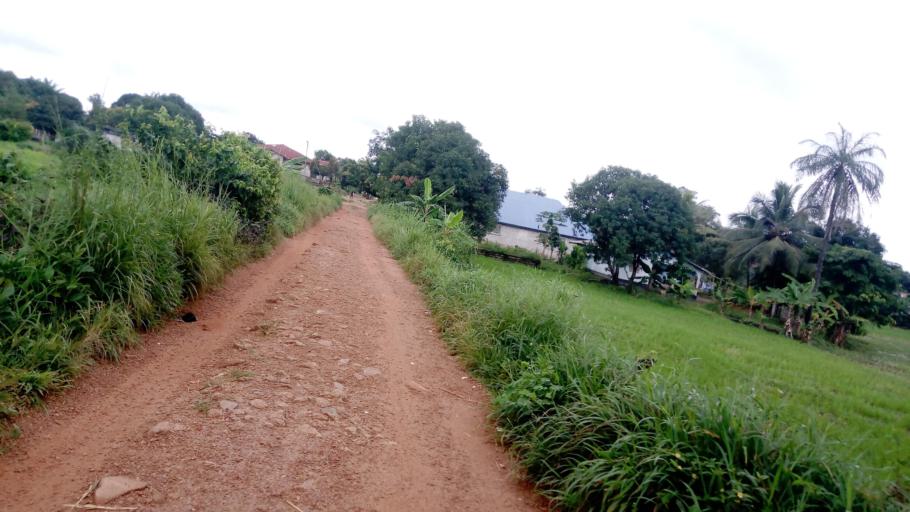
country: SL
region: Northern Province
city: Makeni
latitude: 8.8971
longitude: -12.0308
